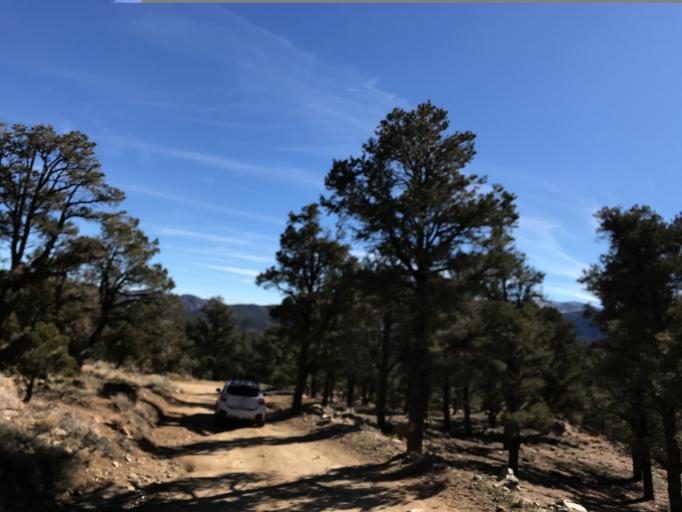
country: US
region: California
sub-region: San Bernardino County
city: Big Bear City
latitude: 34.2719
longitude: -116.7699
